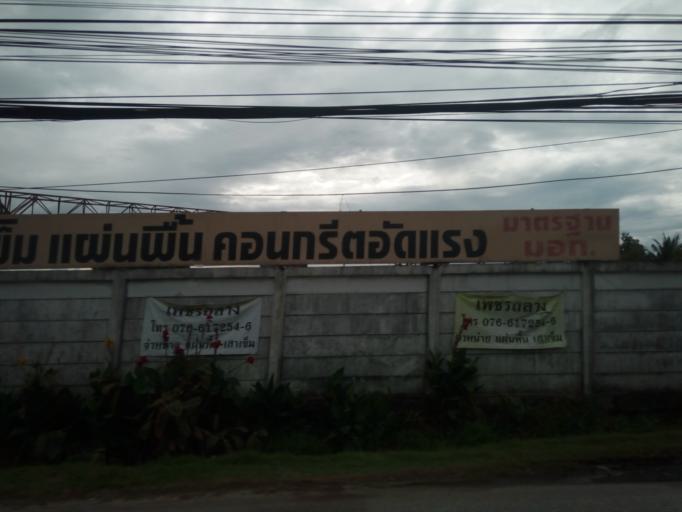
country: TH
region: Phuket
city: Thalang
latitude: 7.9935
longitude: 98.3534
